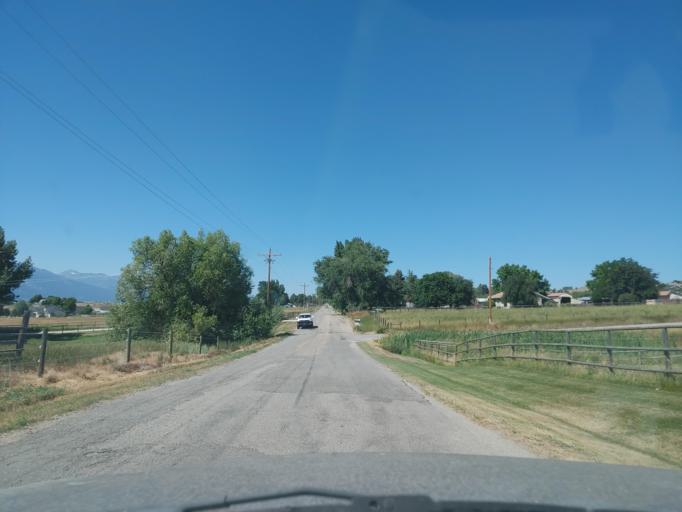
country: US
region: Montana
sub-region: Ravalli County
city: Hamilton
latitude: 46.3338
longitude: -114.0614
